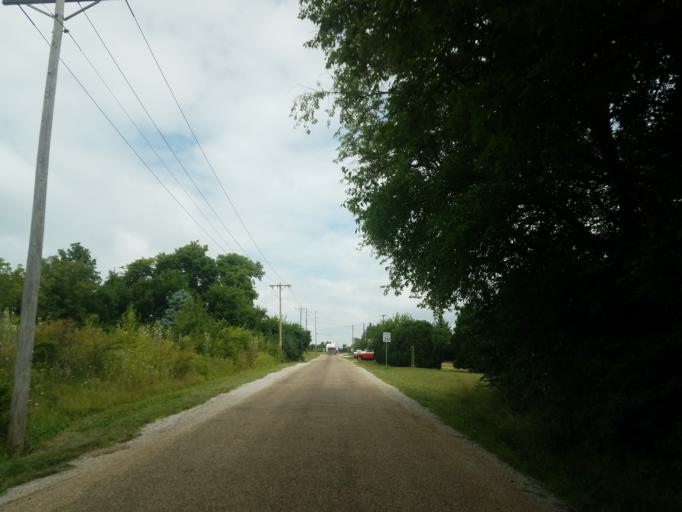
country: US
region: Illinois
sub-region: McLean County
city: Bloomington
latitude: 40.4473
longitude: -89.0151
